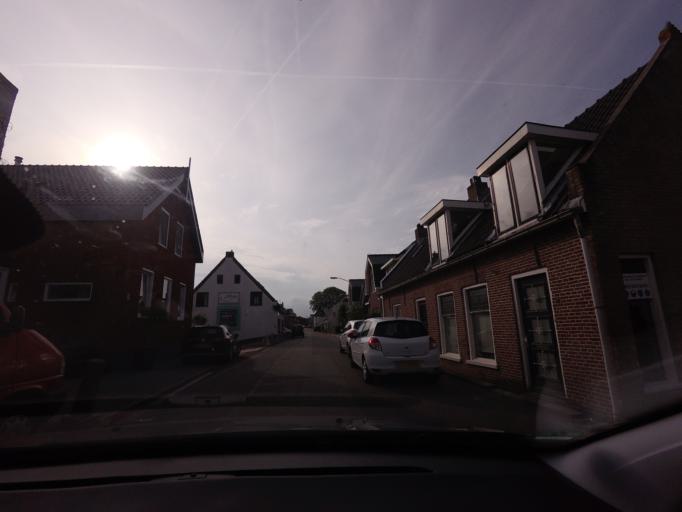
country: NL
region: South Holland
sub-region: Gemeente Papendrecht
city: Papendrecht
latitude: 51.8255
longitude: 4.6819
